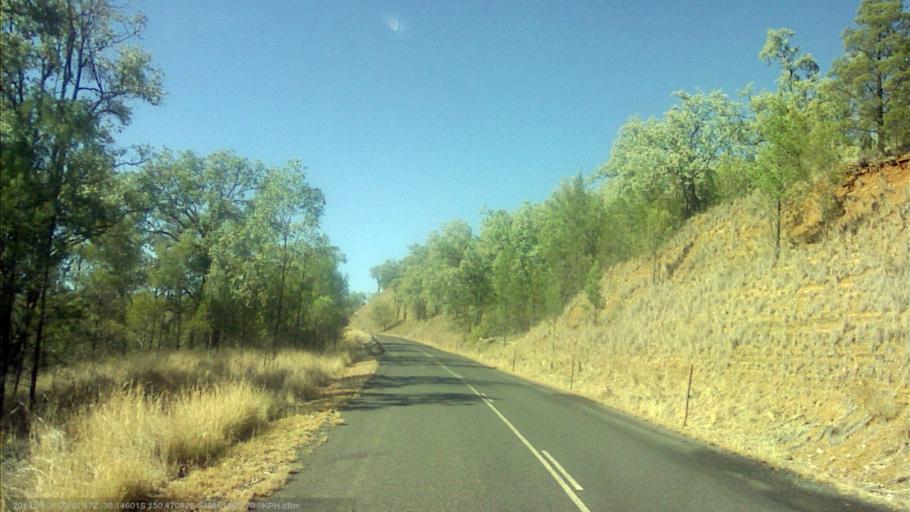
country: AU
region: New South Wales
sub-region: Gwydir
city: Bingara
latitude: -30.1460
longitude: 150.4708
